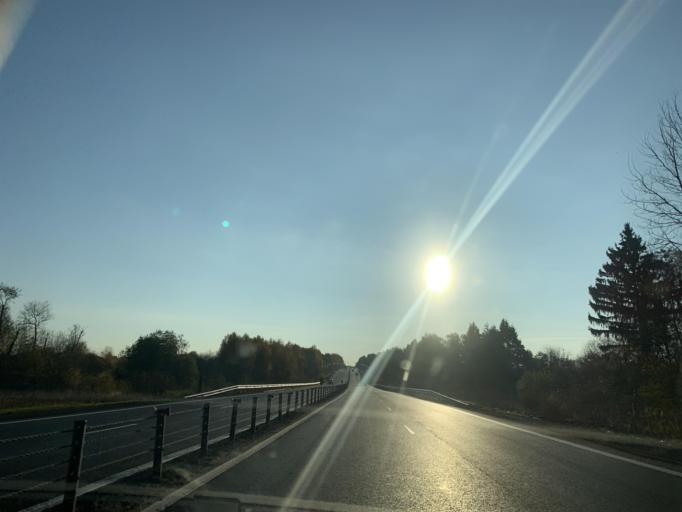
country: RU
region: Jaroslavl
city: Konstantinovskiy
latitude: 57.7794
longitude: 39.6367
